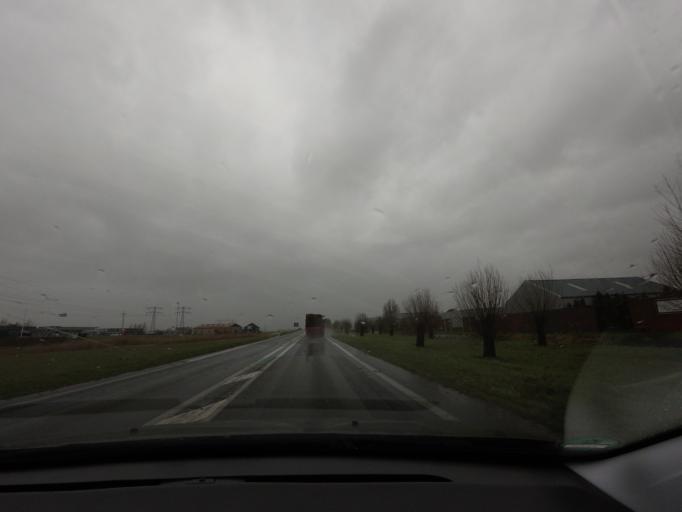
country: NL
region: Friesland
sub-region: Sudwest Fryslan
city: Bolsward
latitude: 53.0655
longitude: 5.5094
